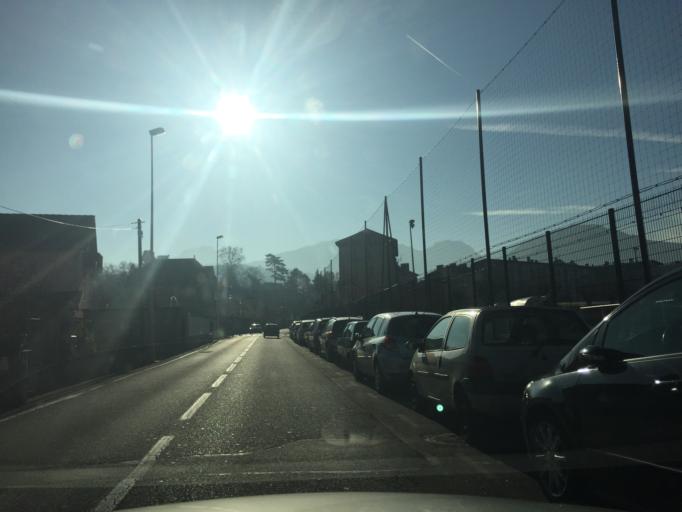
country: FR
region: Rhone-Alpes
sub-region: Departement de la Savoie
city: Jacob-Bellecombette
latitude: 45.5624
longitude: 5.9082
